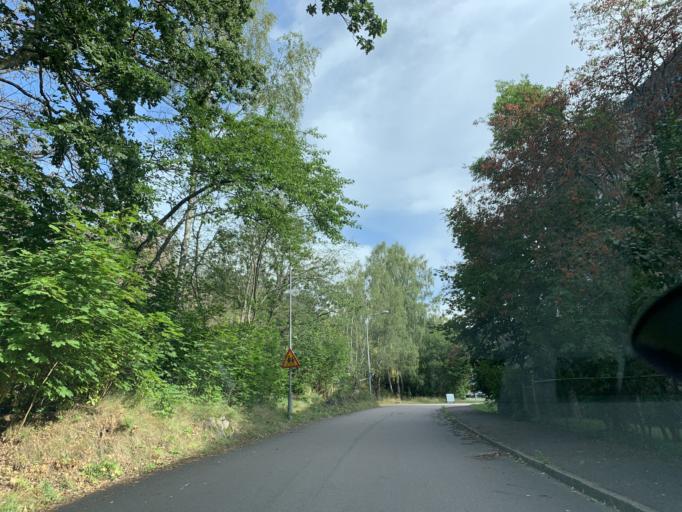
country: SE
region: Vaestra Goetaland
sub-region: Goteborg
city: Hammarkullen
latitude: 57.7703
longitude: 12.0138
